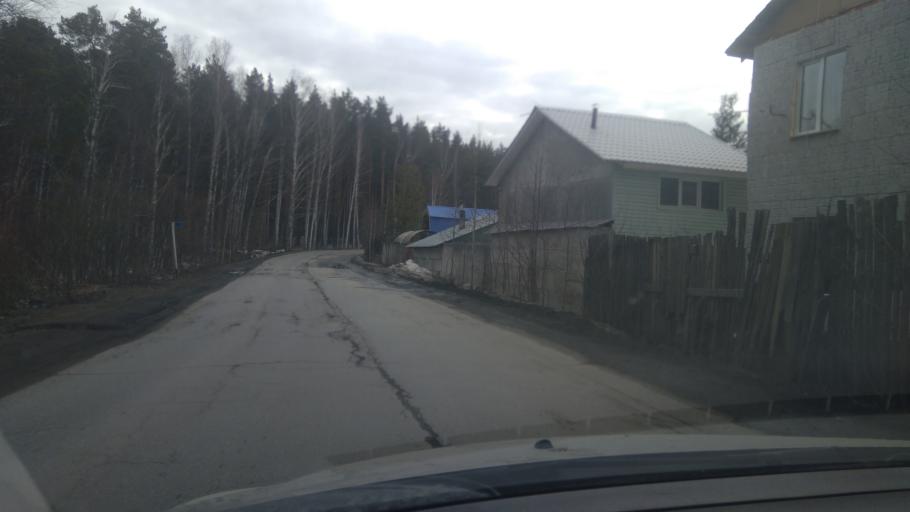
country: RU
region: Sverdlovsk
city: Severka
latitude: 56.8415
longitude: 60.3854
